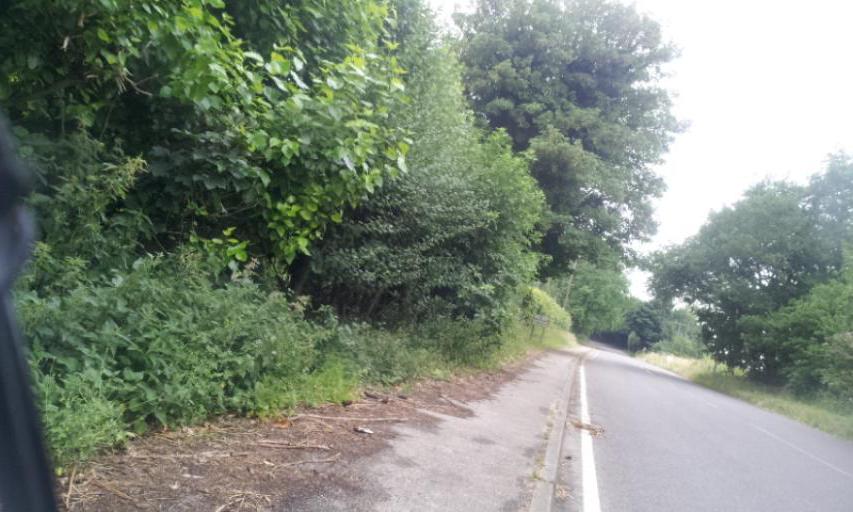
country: GB
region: England
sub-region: Kent
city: Sittingbourne
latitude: 51.3162
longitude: 0.7037
